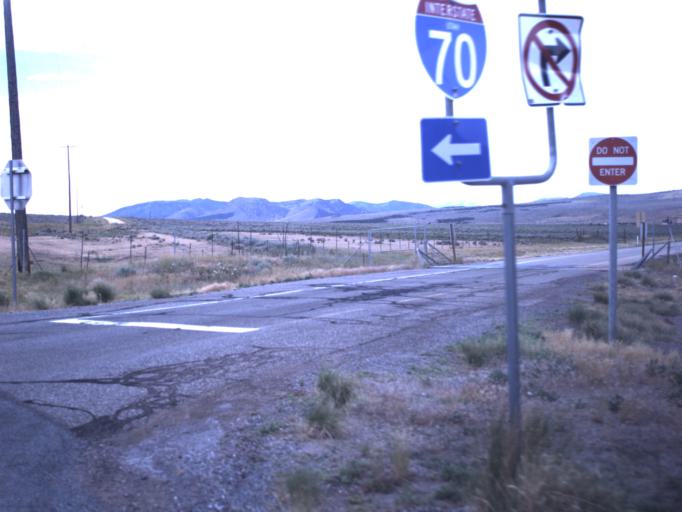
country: US
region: Utah
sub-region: Beaver County
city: Beaver
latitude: 38.5864
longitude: -112.5846
